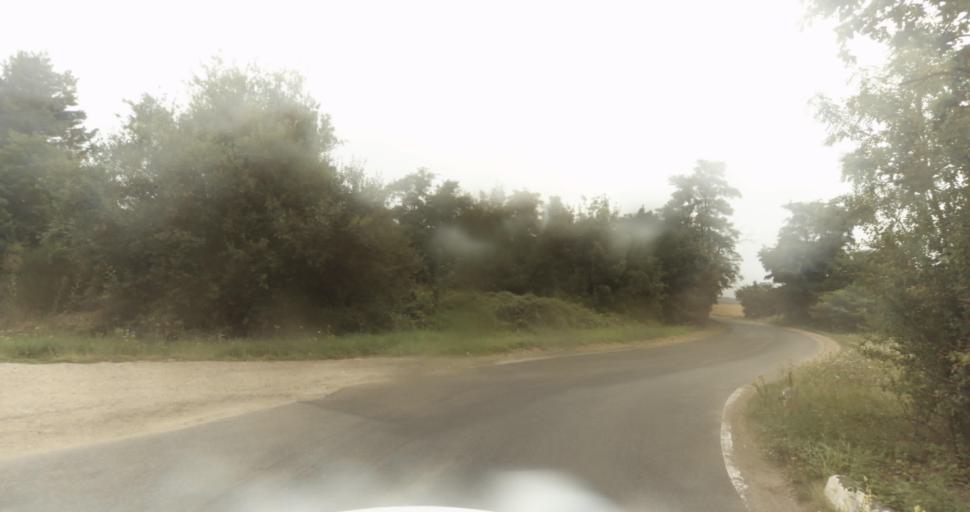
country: FR
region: Centre
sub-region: Departement d'Eure-et-Loir
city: Saint-Lubin-des-Joncherets
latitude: 48.7746
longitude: 1.2162
